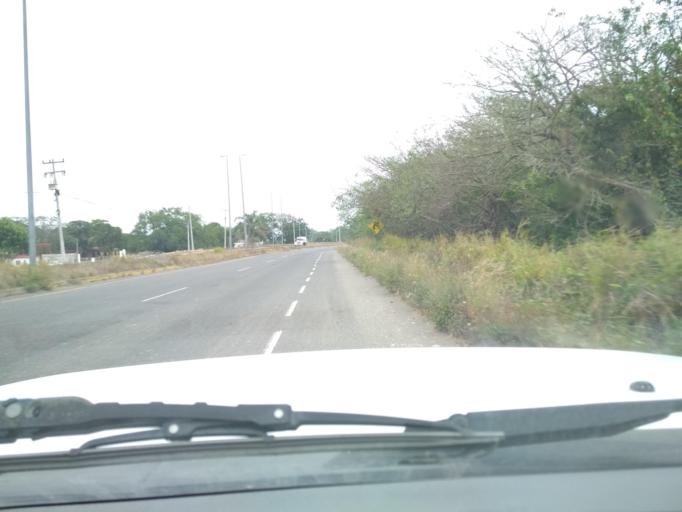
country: MX
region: Veracruz
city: El Tejar
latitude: 19.0666
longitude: -96.1312
